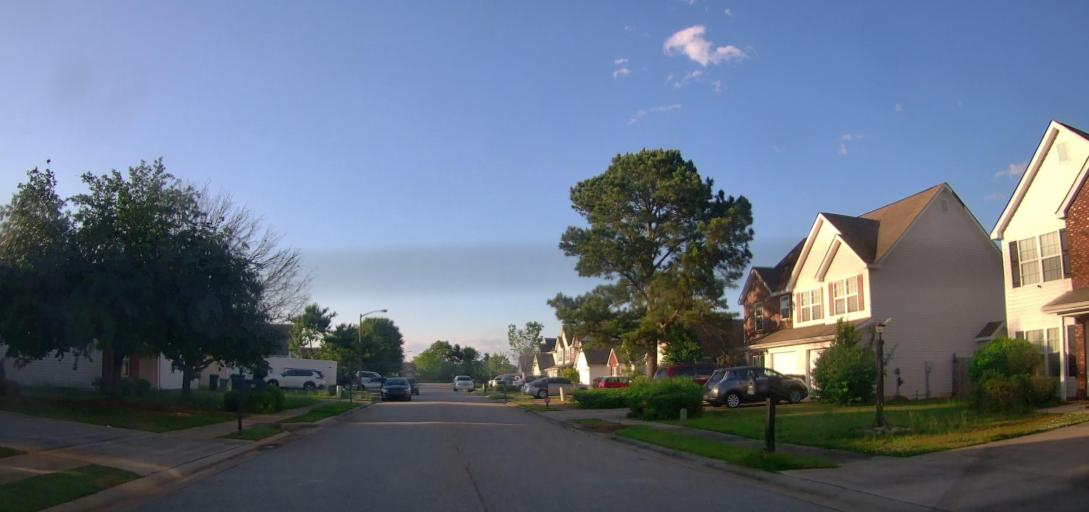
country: US
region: Georgia
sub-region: Houston County
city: Centerville
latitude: 32.6293
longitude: -83.7135
